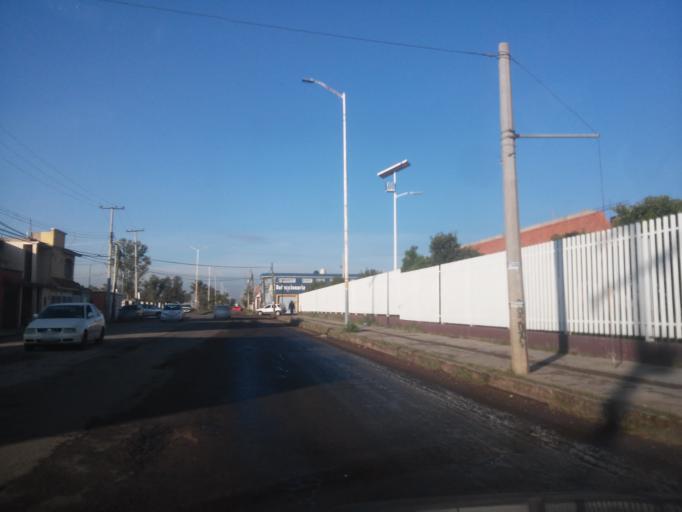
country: MX
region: Durango
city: Victoria de Durango
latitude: 24.0504
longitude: -104.6108
